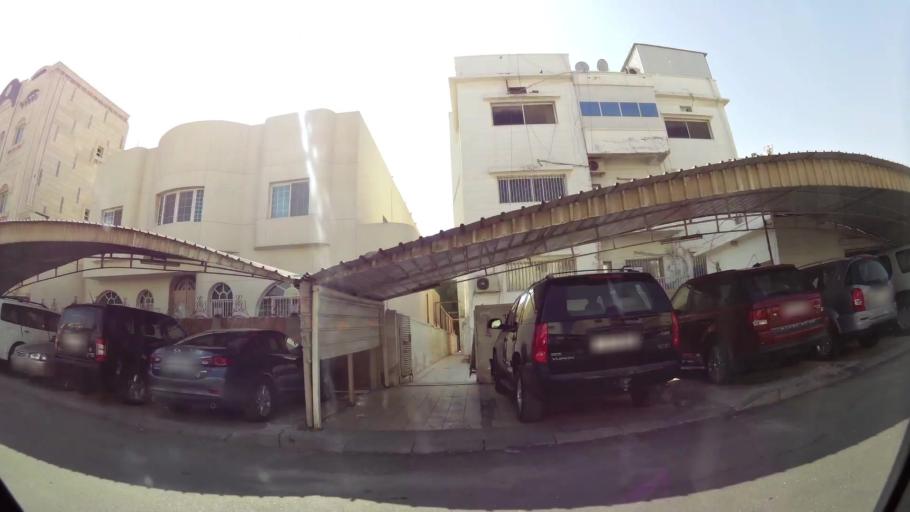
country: KW
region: Muhafazat Hawalli
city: Salwa
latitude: 29.2765
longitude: 48.0821
